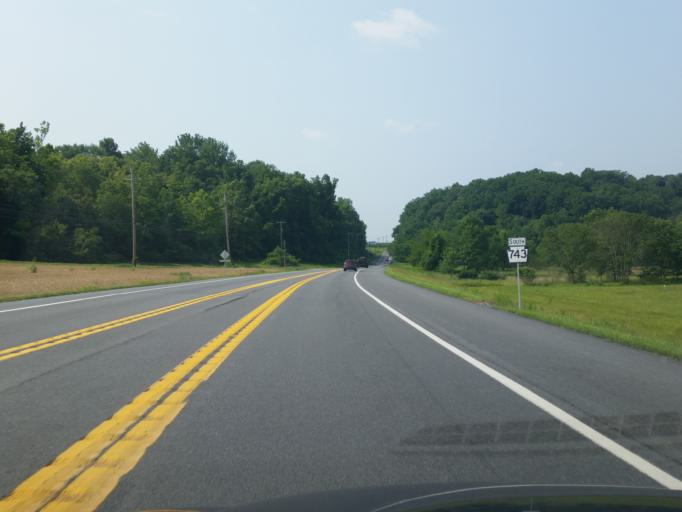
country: US
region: Pennsylvania
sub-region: Dauphin County
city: Palmdale
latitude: 40.3131
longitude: -76.6294
